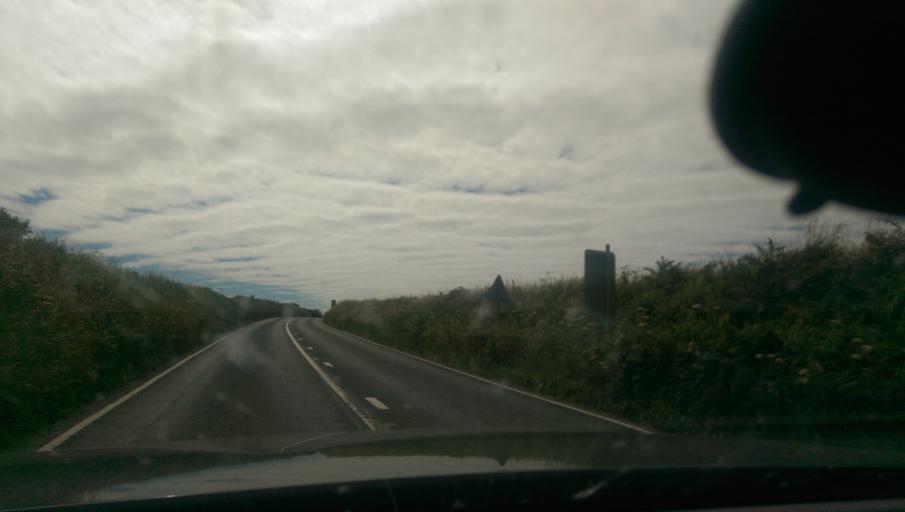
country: GB
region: England
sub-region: Cornwall
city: Wadebridge
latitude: 50.5114
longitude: -4.8745
